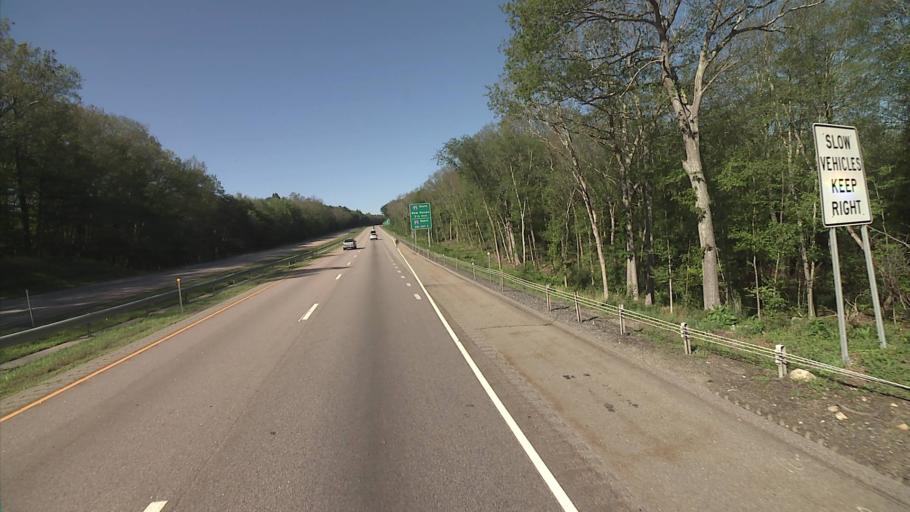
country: US
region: Connecticut
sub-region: New London County
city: Oxoboxo River
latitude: 41.4086
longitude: -72.1446
